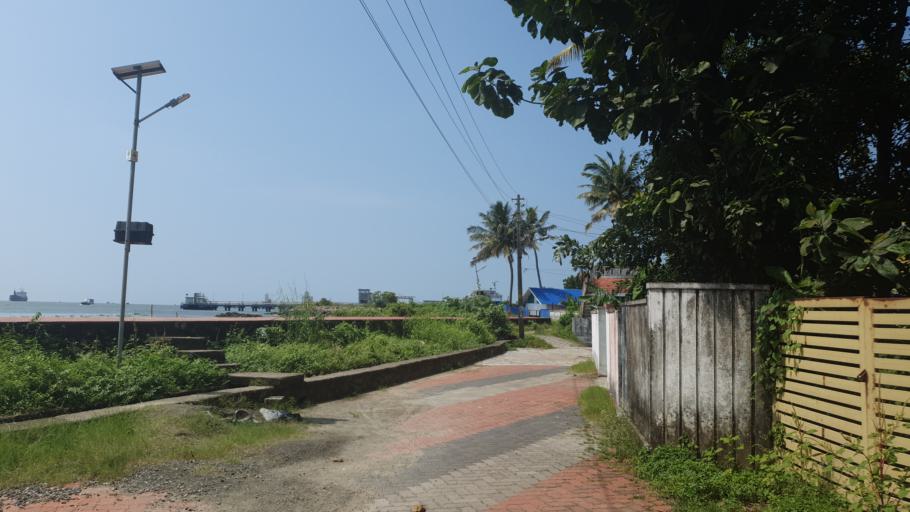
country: IN
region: Kerala
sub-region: Ernakulam
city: Cochin
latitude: 9.9729
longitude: 76.2408
